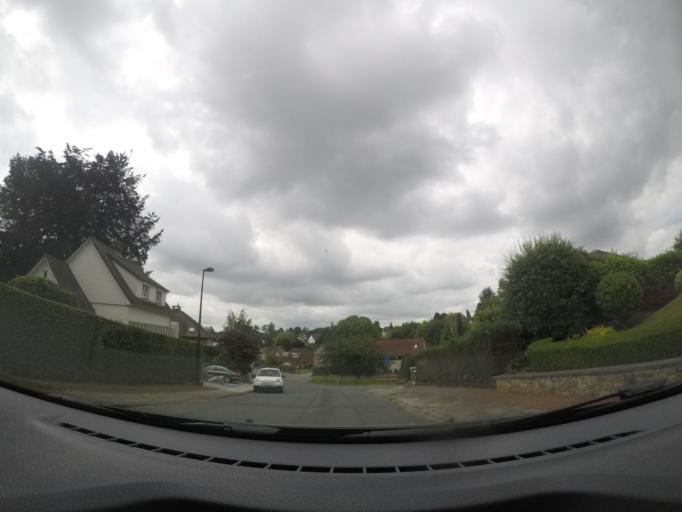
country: BE
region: Flanders
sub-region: Provincie Vlaams-Brabant
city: Sint-Genesius-Rode
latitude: 50.7539
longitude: 4.3471
